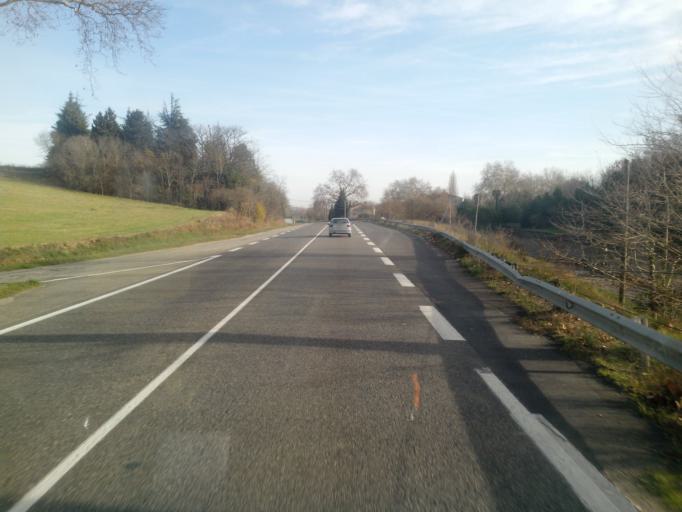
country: FR
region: Languedoc-Roussillon
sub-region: Departement de l'Aude
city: Saint-Martin-Lalande
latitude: 43.2986
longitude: 1.9915
